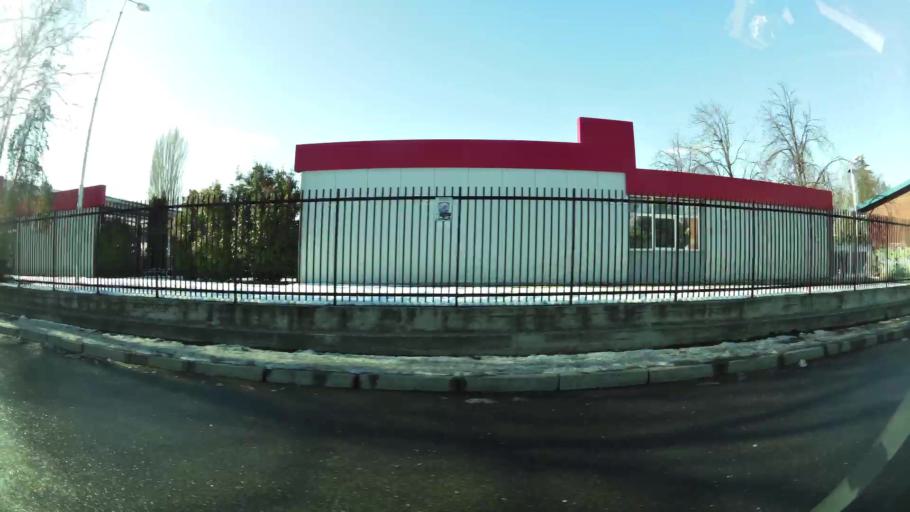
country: MK
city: Krushopek
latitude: 42.0054
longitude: 21.3746
